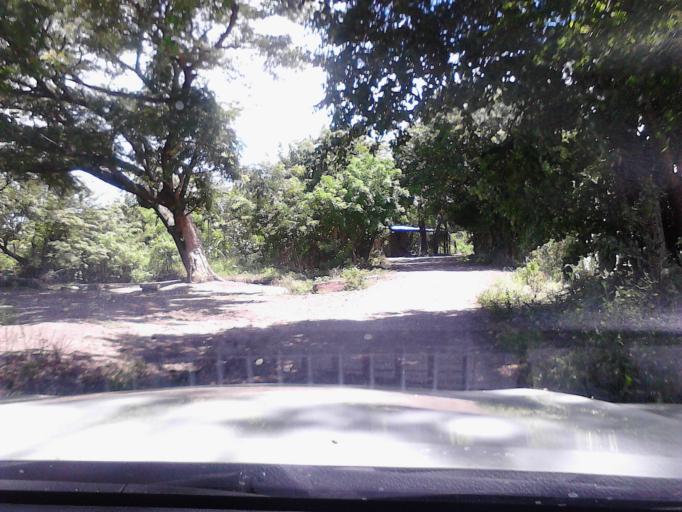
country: NI
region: Matagalpa
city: Ciudad Dario
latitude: 12.8977
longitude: -86.1424
